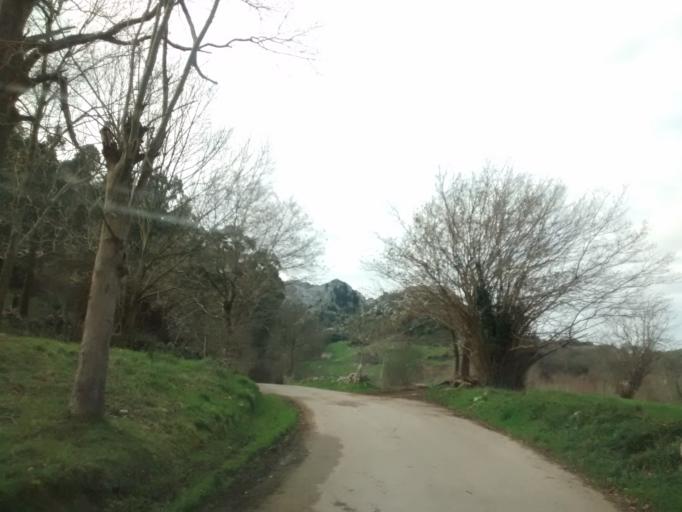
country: ES
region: Cantabria
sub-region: Provincia de Cantabria
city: Entrambasaguas
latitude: 43.3414
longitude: -3.7000
